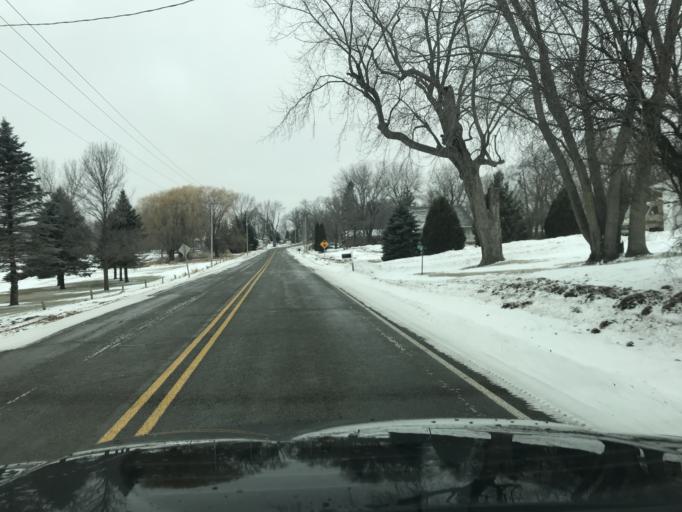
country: US
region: Wisconsin
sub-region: Dane County
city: Cottage Grove
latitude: 43.0868
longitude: -89.2333
